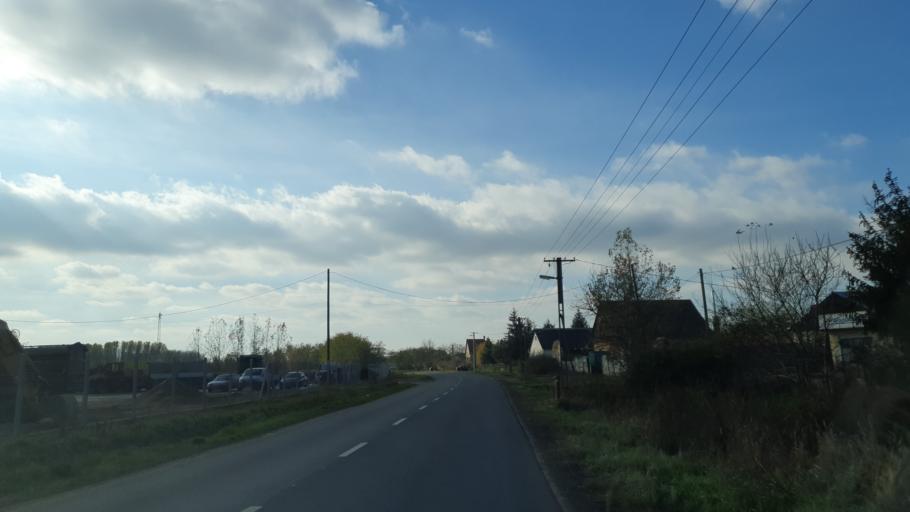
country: HU
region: Szabolcs-Szatmar-Bereg
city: Nyirkarasz
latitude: 48.0921
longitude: 22.0953
